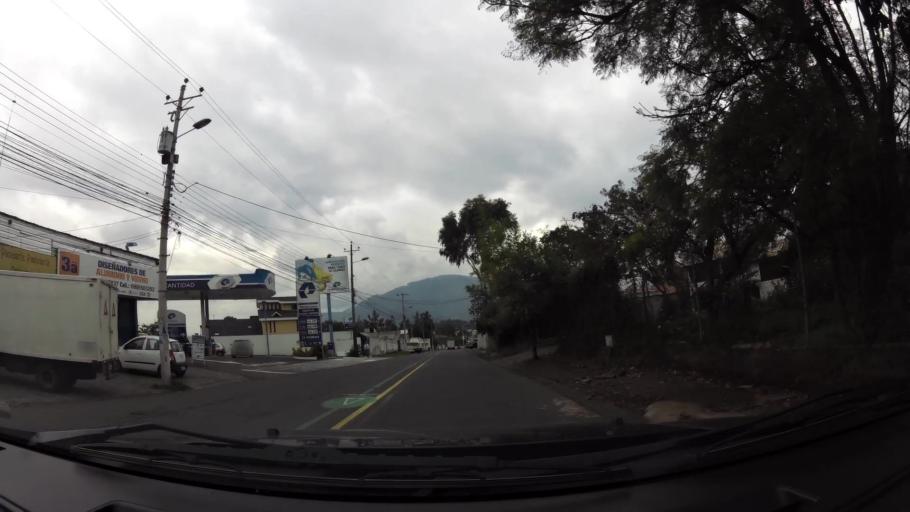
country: EC
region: Pichincha
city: Sangolqui
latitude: -0.3035
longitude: -78.4659
